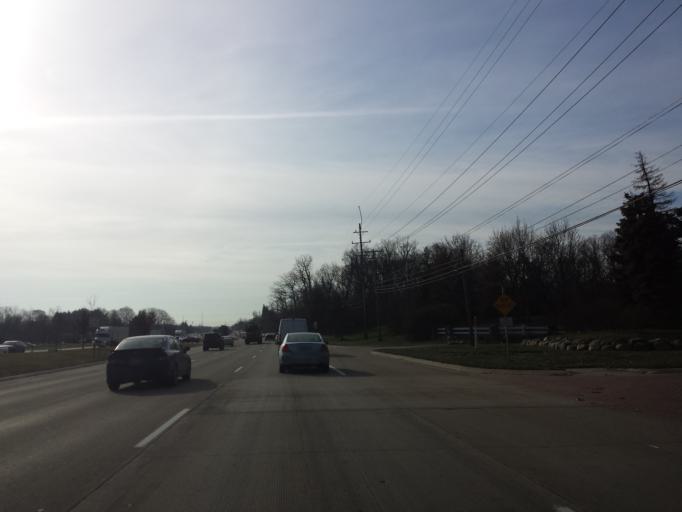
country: US
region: Michigan
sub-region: Oakland County
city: Bingham Farms
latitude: 42.5225
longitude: -83.2860
